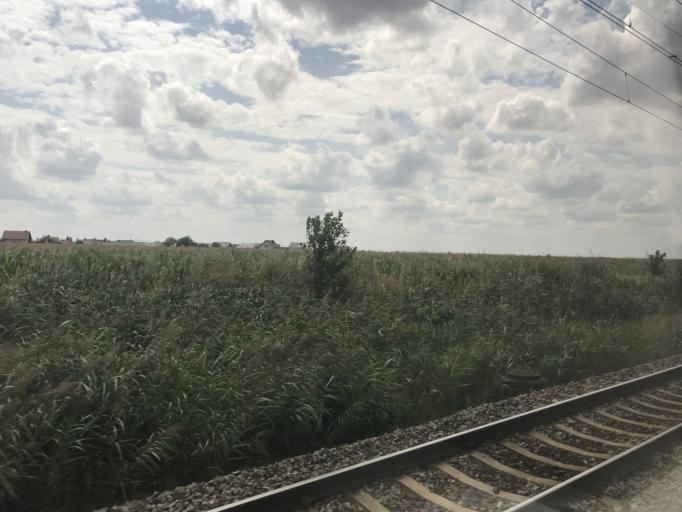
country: PL
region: Greater Poland Voivodeship
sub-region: Powiat poznanski
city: Buk
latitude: 52.3404
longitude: 16.5101
